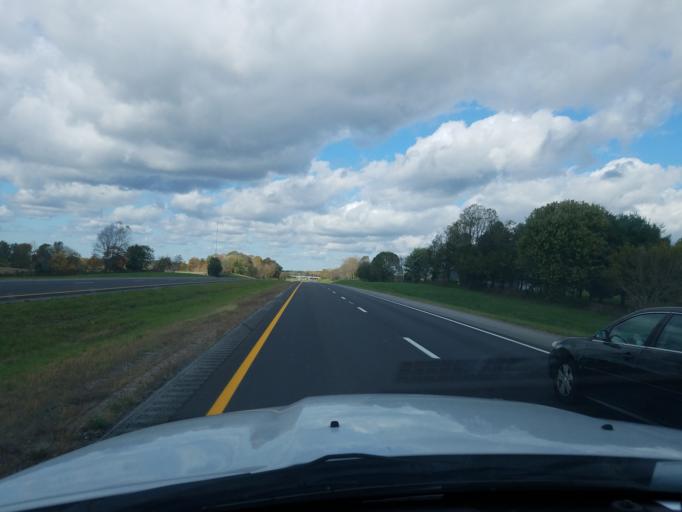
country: US
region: Kentucky
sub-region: Russell County
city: Russell Springs
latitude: 37.0503
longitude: -85.1539
